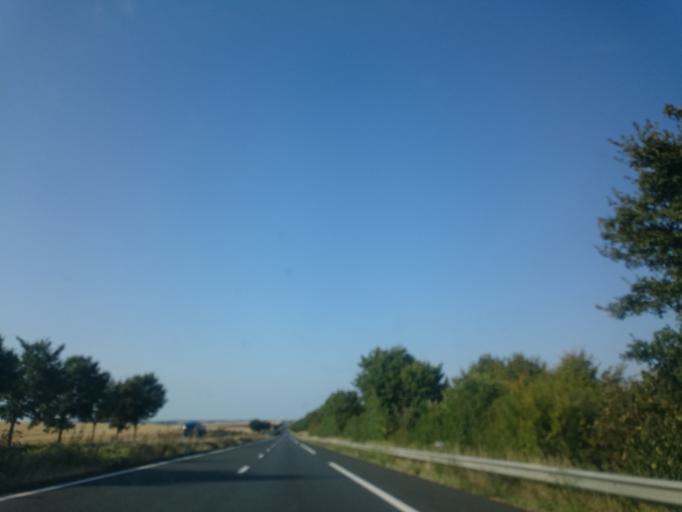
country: FR
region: Centre
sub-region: Departement de l'Indre
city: Vatan
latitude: 47.0008
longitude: 1.7774
